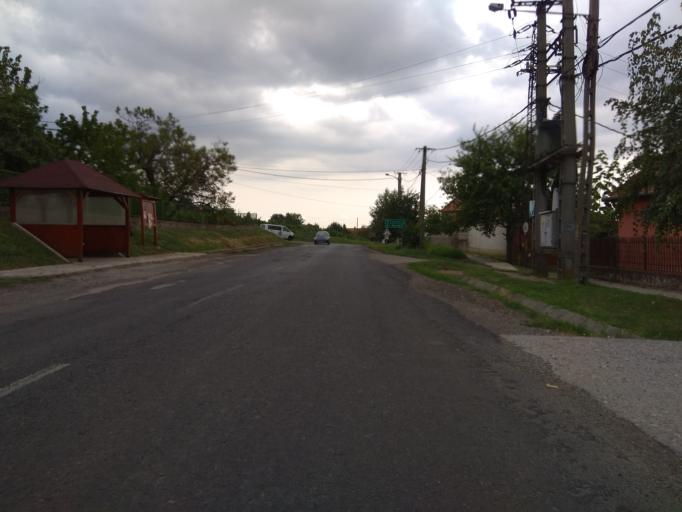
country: HU
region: Borsod-Abauj-Zemplen
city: Bekecs
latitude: 48.1543
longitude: 21.1624
